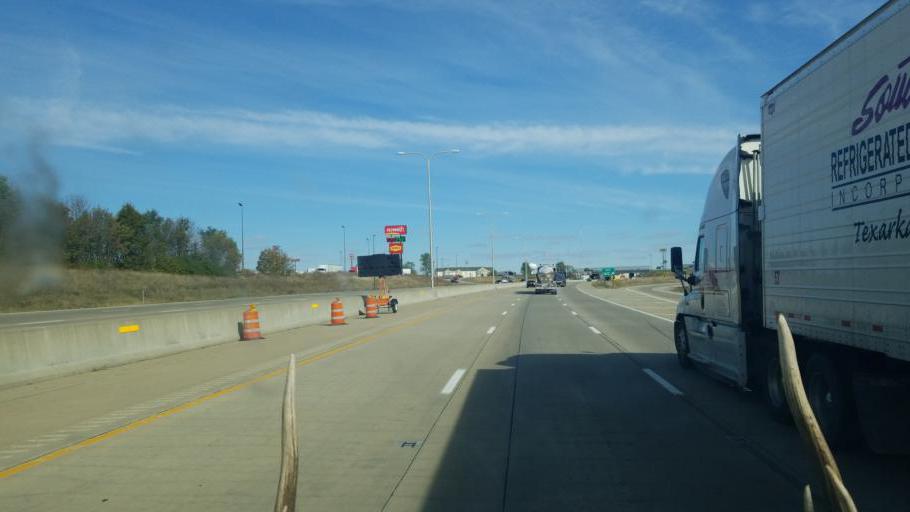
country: US
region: Illinois
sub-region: Effingham County
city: Effingham
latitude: 39.1300
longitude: -88.5654
